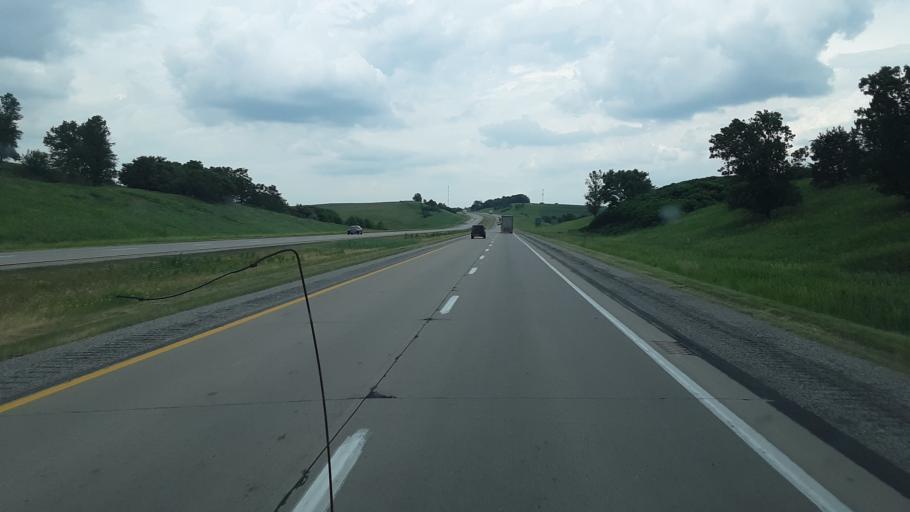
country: US
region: Iowa
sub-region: Pottawattamie County
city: Oakland
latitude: 41.4711
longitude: -95.5923
